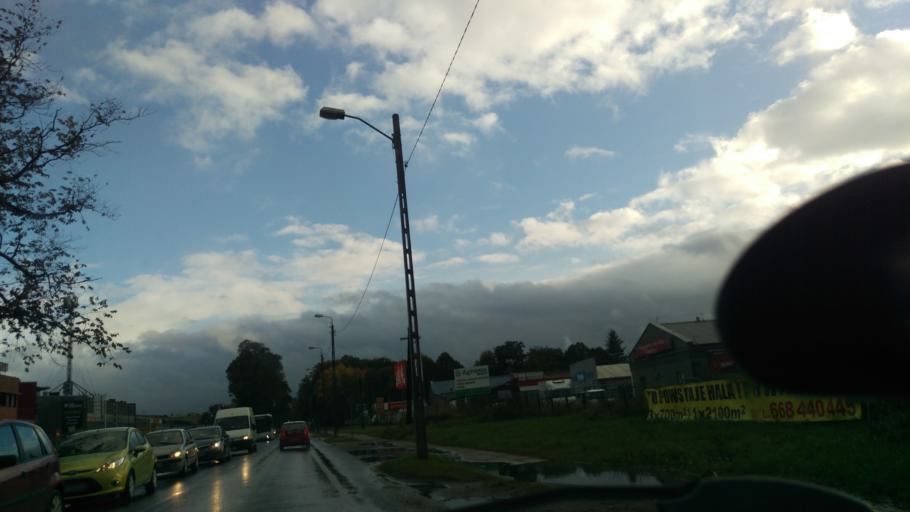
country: PL
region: West Pomeranian Voivodeship
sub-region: Szczecin
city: Szczecin
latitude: 53.3910
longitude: 14.6748
